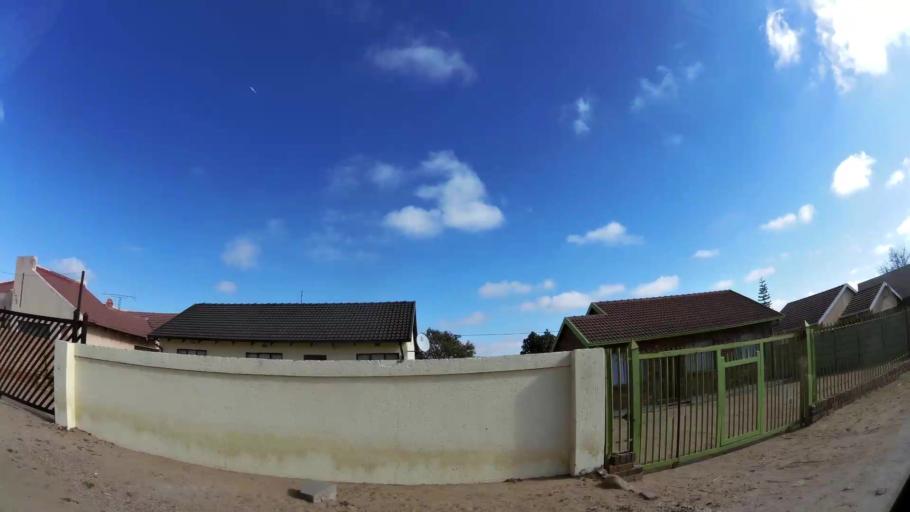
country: ZA
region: Limpopo
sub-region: Capricorn District Municipality
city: Polokwane
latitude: -23.8562
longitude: 29.3749
